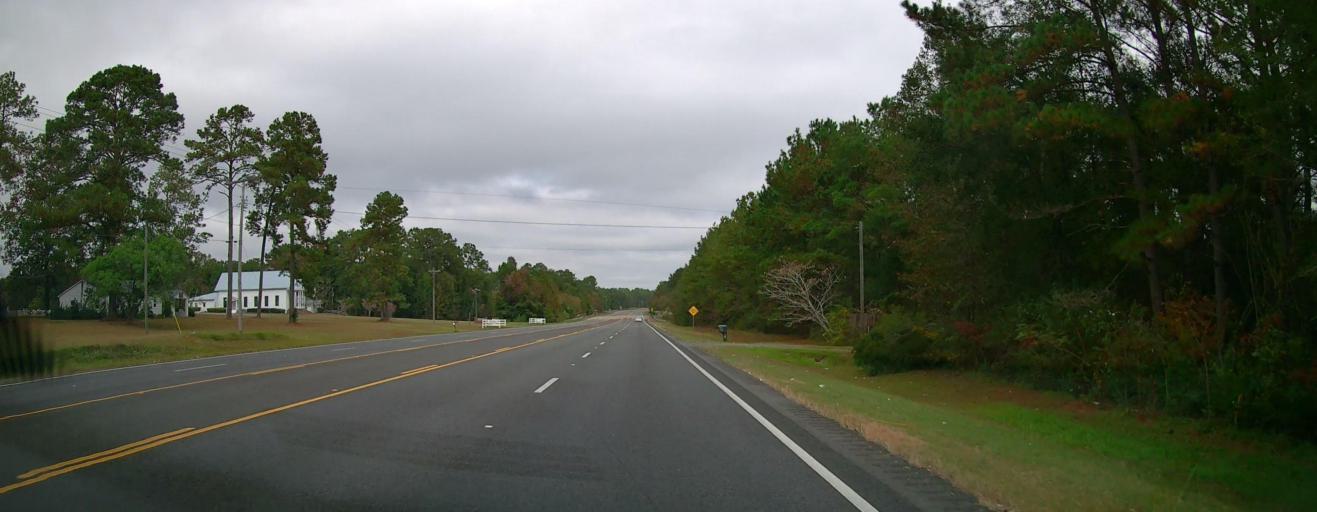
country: US
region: Georgia
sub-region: Thomas County
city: Thomasville
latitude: 30.9711
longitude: -83.8902
